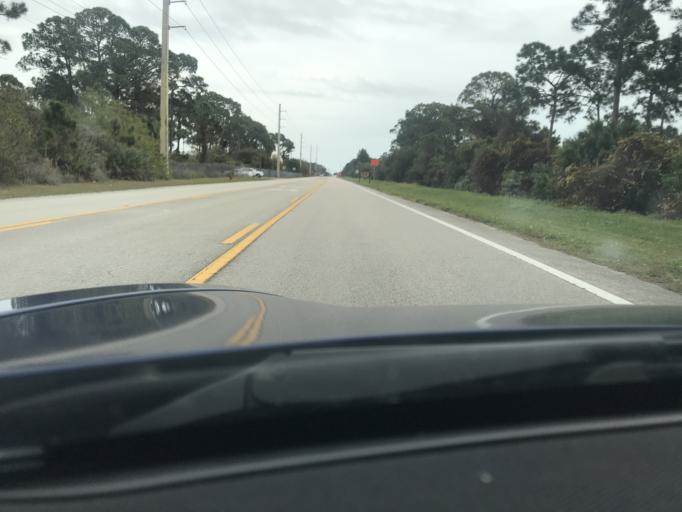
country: US
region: Florida
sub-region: Indian River County
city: Winter Beach
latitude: 27.7338
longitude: -80.4505
